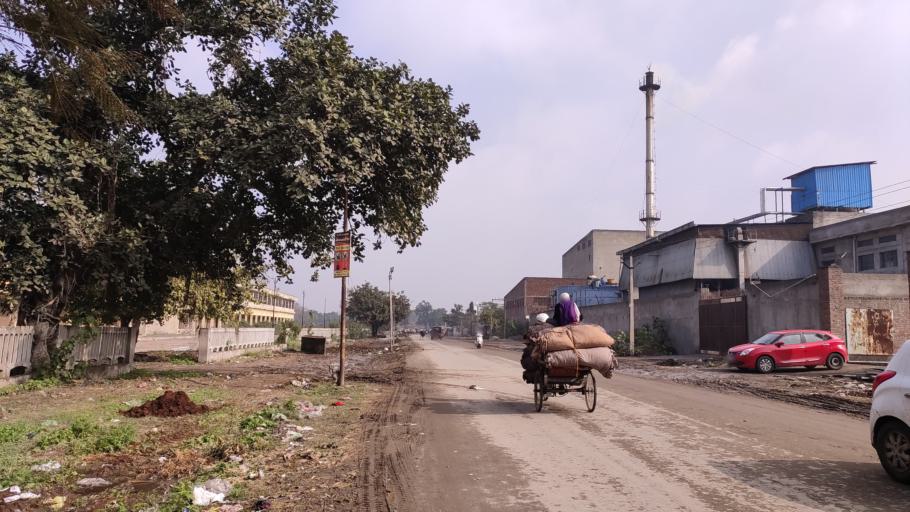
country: IN
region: Punjab
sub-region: Amritsar
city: Amritsar
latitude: 31.6240
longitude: 74.9134
